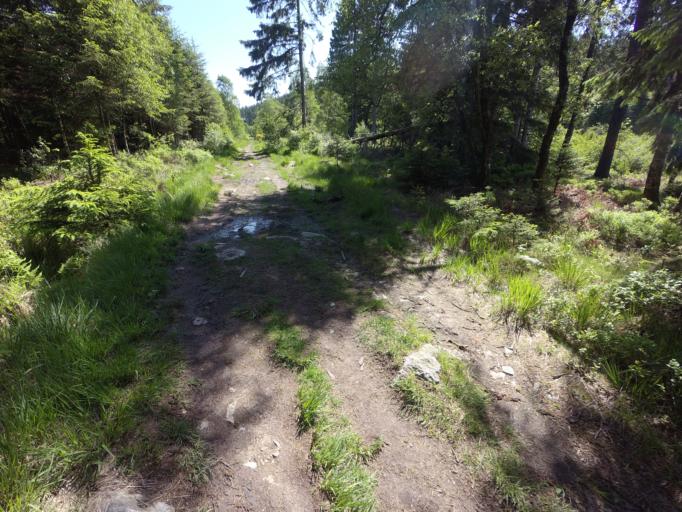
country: BE
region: Wallonia
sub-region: Province de Liege
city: Malmedy
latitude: 50.4999
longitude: 6.0526
